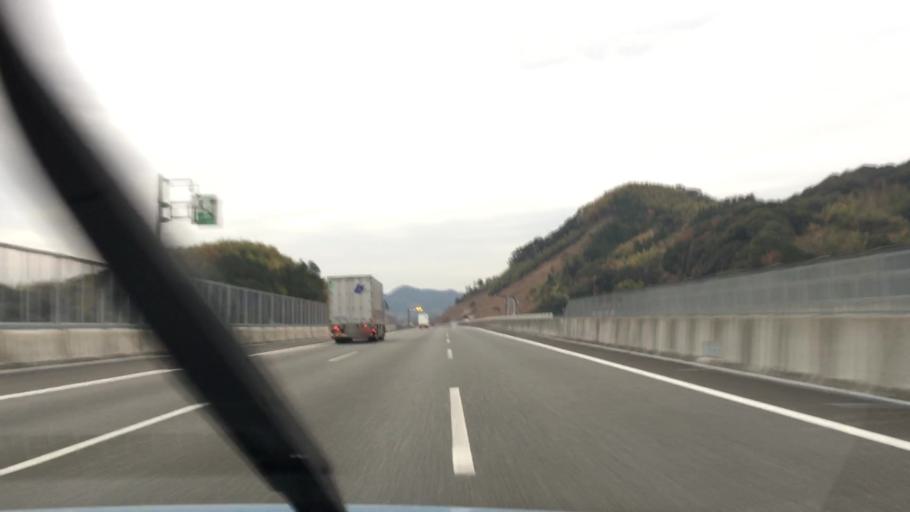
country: JP
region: Shizuoka
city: Fujieda
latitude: 34.9155
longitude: 138.2610
